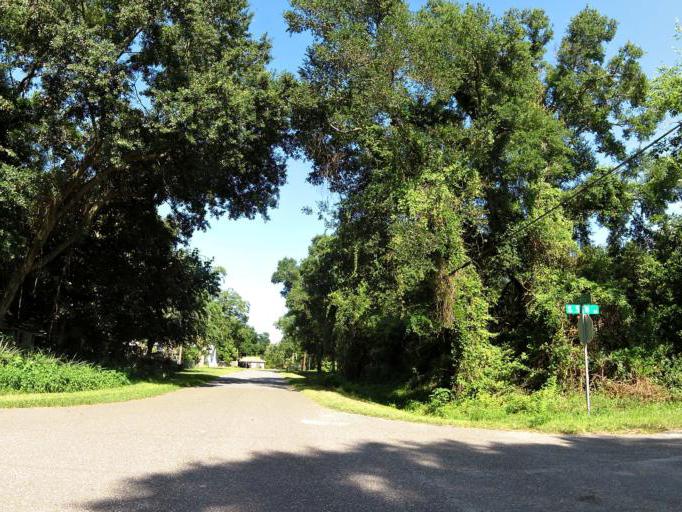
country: US
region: Florida
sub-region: Nassau County
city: Fernandina Beach
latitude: 30.6547
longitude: -81.4638
